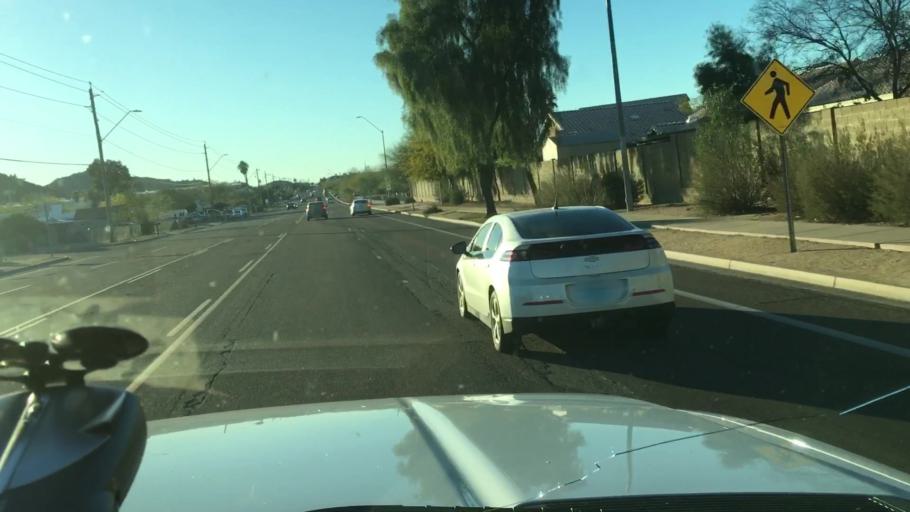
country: US
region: Arizona
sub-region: Maricopa County
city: Paradise Valley
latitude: 33.6697
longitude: -112.0226
